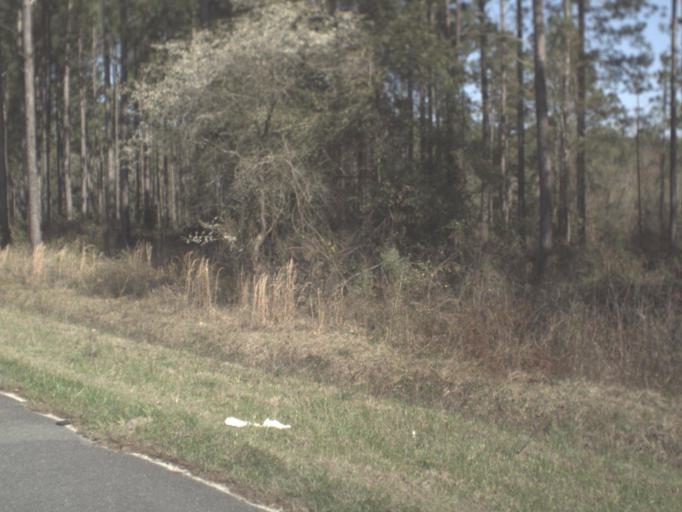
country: US
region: Florida
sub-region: Gulf County
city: Wewahitchka
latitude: 30.2130
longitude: -85.2074
